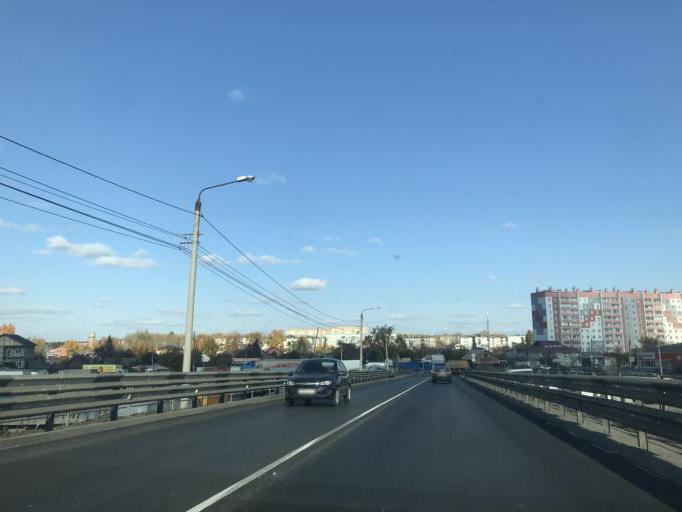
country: RU
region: Chelyabinsk
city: Roshchino
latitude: 55.2347
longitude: 61.2955
